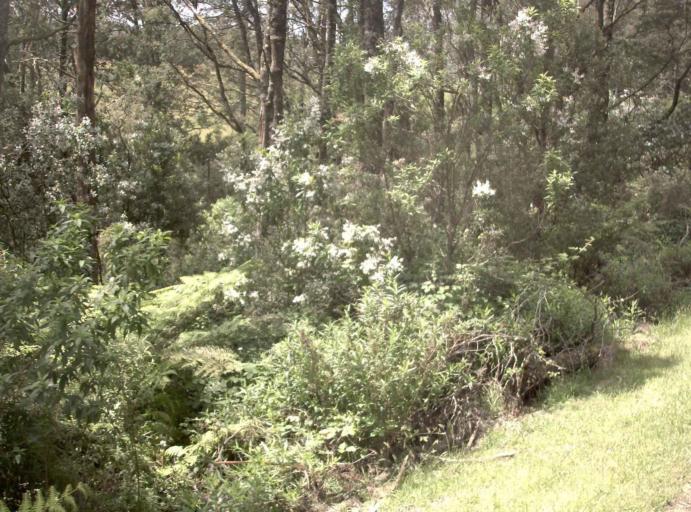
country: AU
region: Victoria
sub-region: Latrobe
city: Traralgon
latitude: -38.4301
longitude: 146.5603
